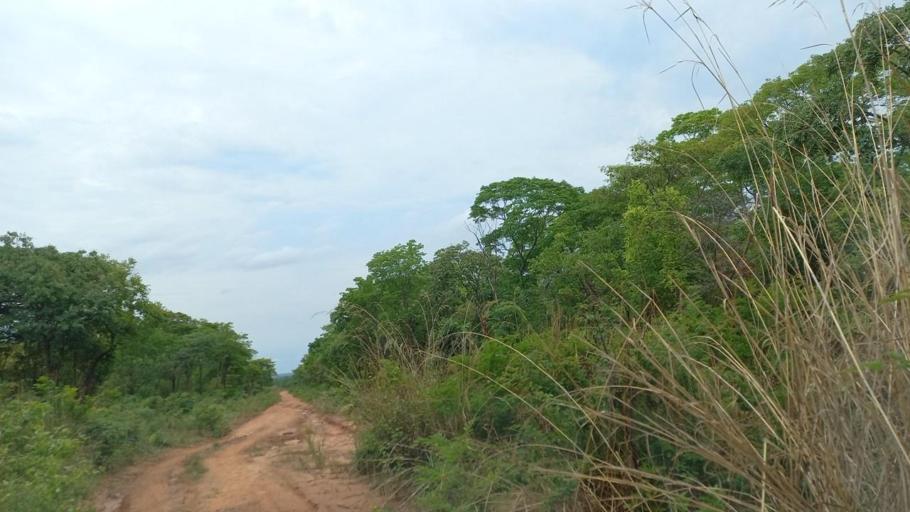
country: ZM
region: North-Western
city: Kalengwa
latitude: -13.6207
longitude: 24.9767
